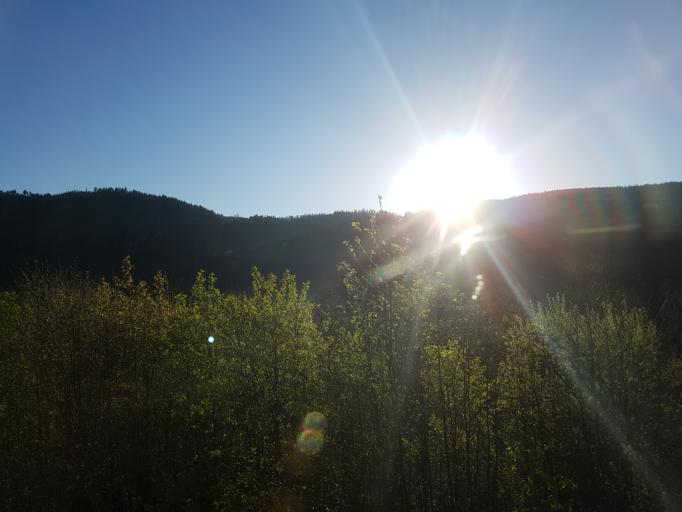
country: NO
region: Sor-Trondelag
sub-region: Midtre Gauldal
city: Storen
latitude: 63.0394
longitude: 10.2897
